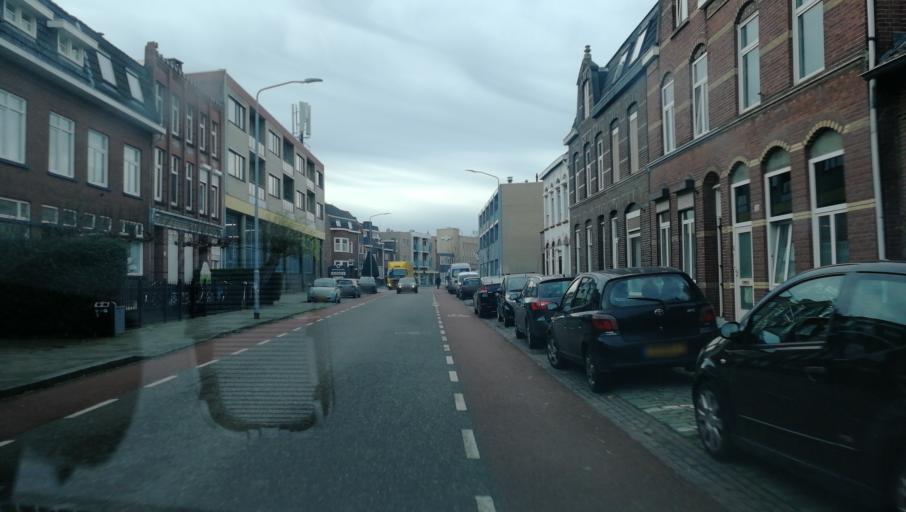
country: NL
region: Limburg
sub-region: Gemeente Venlo
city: Venlo
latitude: 51.3742
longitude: 6.1768
